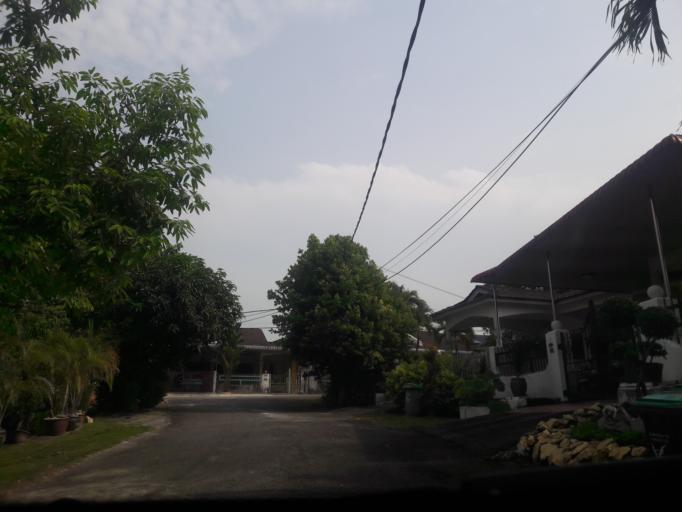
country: MY
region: Kedah
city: Kulim
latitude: 5.3591
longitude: 100.5312
